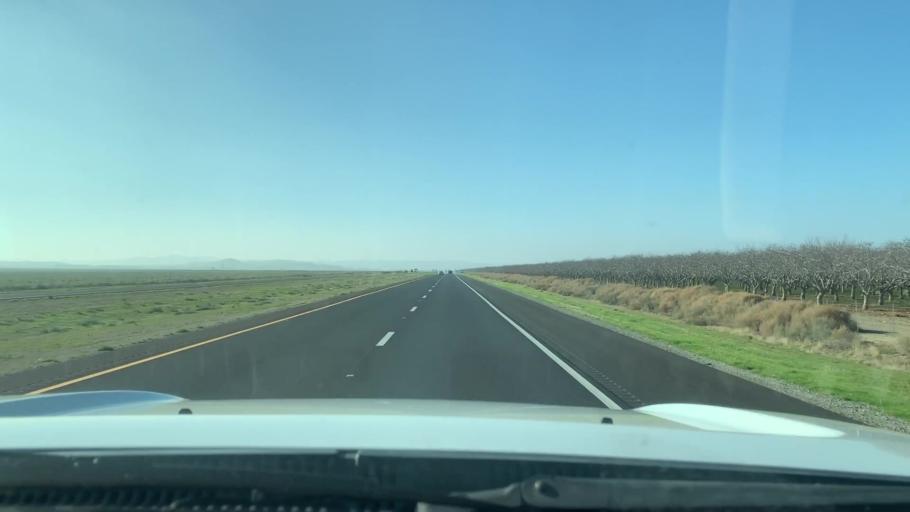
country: US
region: California
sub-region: Kern County
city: Lost Hills
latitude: 35.6148
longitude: -119.9145
